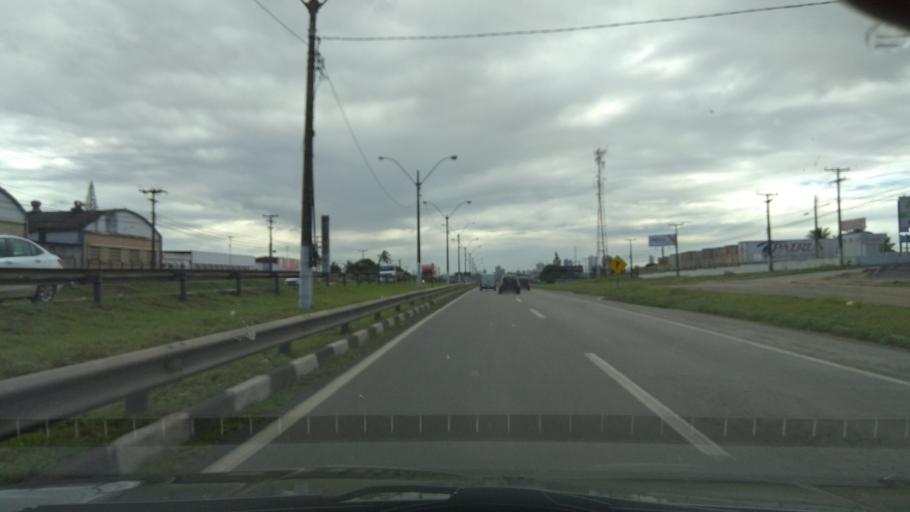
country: BR
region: Bahia
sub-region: Feira De Santana
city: Feira de Santana
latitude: -12.2820
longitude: -38.9225
